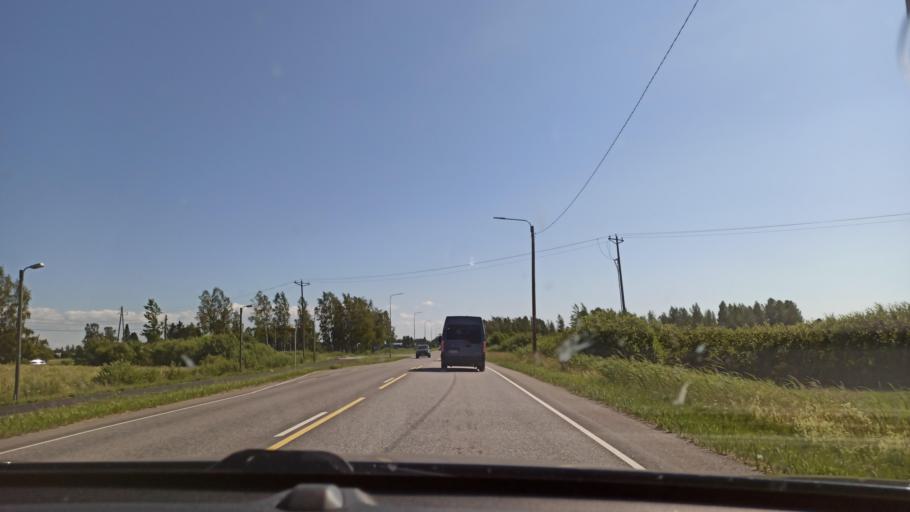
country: FI
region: Satakunta
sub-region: Pori
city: Pori
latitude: 61.5196
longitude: 21.8031
